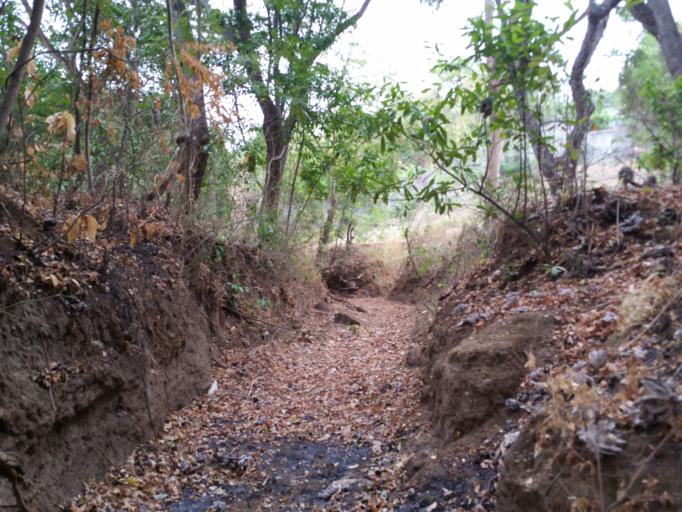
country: NI
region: Managua
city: Managua
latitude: 12.0878
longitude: -86.2491
